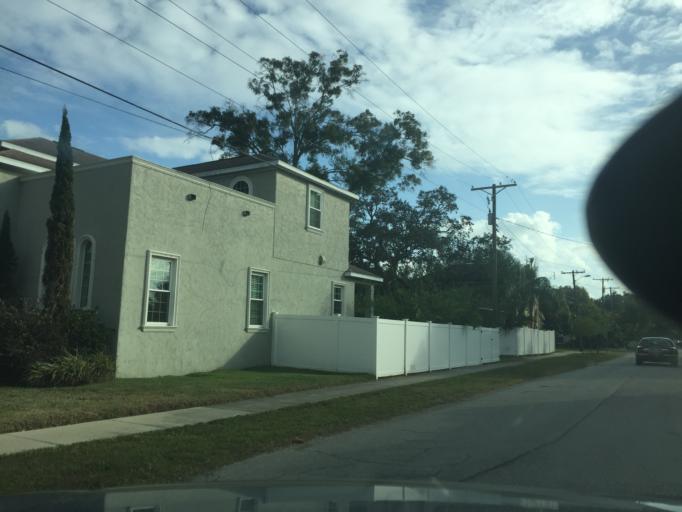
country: US
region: Florida
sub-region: Hillsborough County
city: Tampa
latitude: 27.9484
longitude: -82.4892
